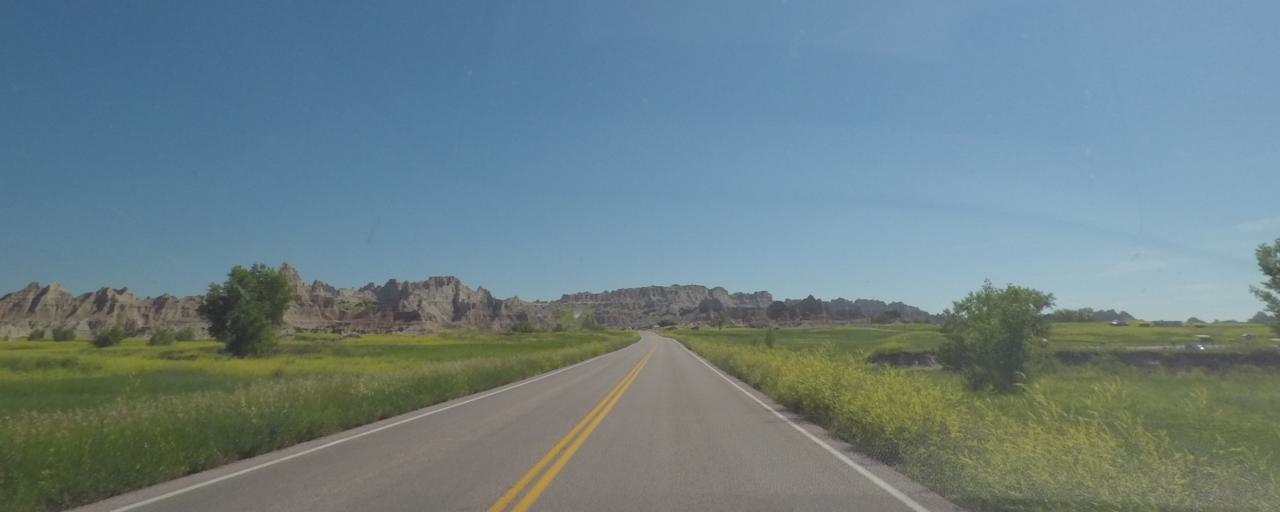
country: US
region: South Dakota
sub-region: Haakon County
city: Philip
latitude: 43.7445
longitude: -101.9525
